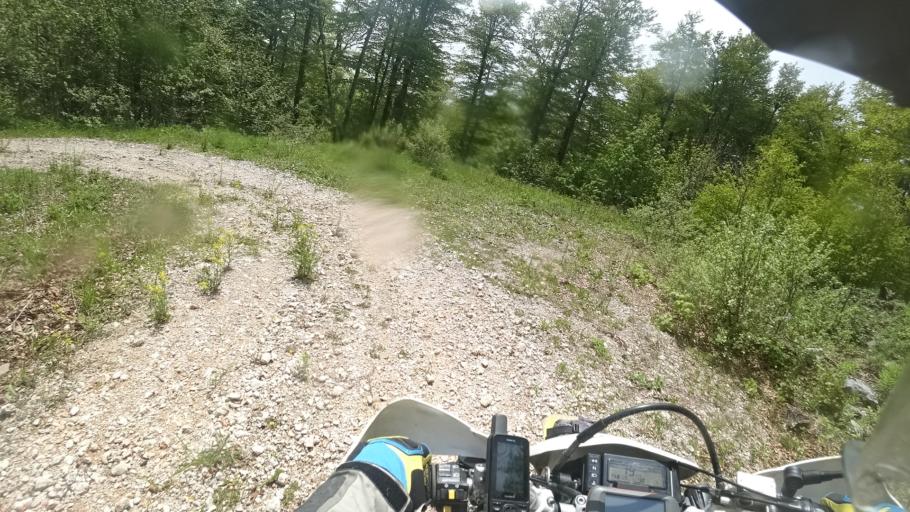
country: BA
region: Federation of Bosnia and Herzegovina
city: Orasac
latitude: 44.5679
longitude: 15.8778
